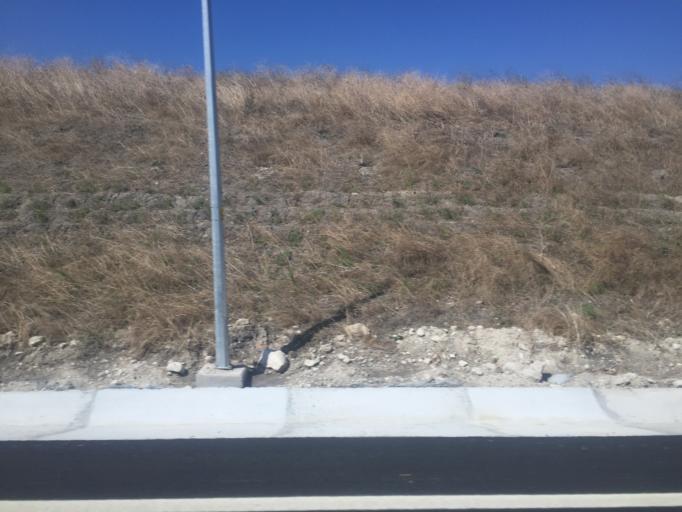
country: TR
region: Balikesir
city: Susurluk
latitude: 39.9639
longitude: 28.1643
